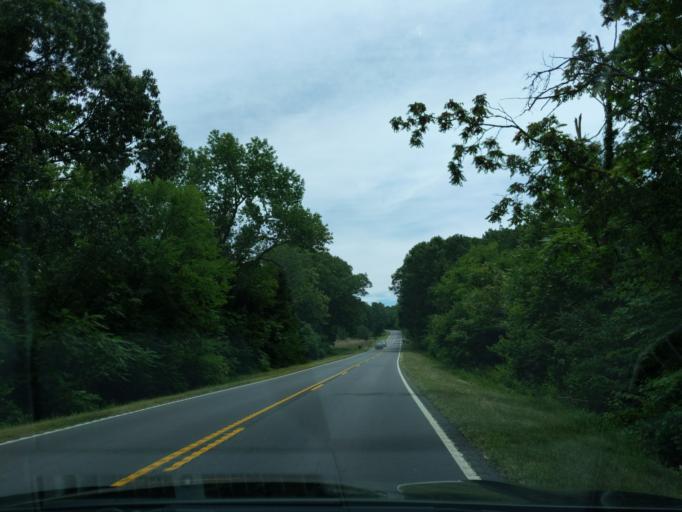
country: US
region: North Carolina
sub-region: Cabarrus County
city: Mount Pleasant
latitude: 35.4376
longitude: -80.3888
